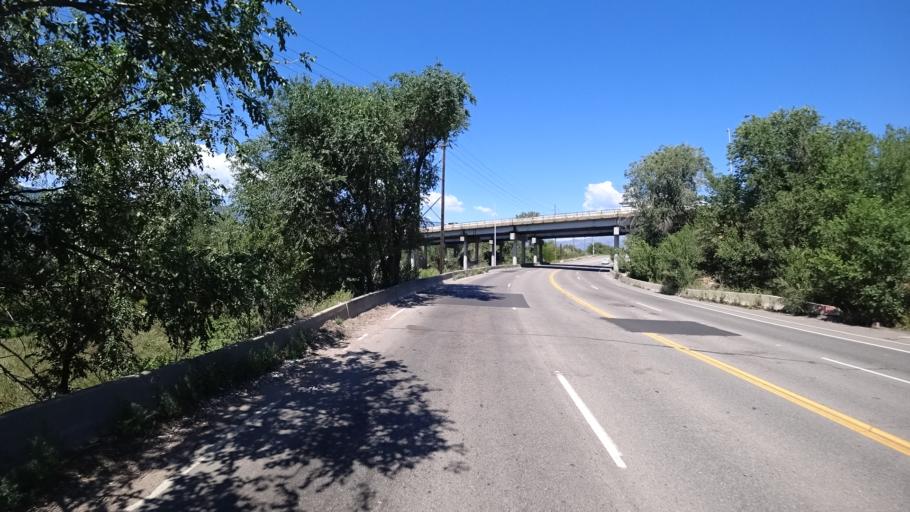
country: US
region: Colorado
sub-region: El Paso County
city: Stratmoor
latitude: 38.7979
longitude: -104.7833
